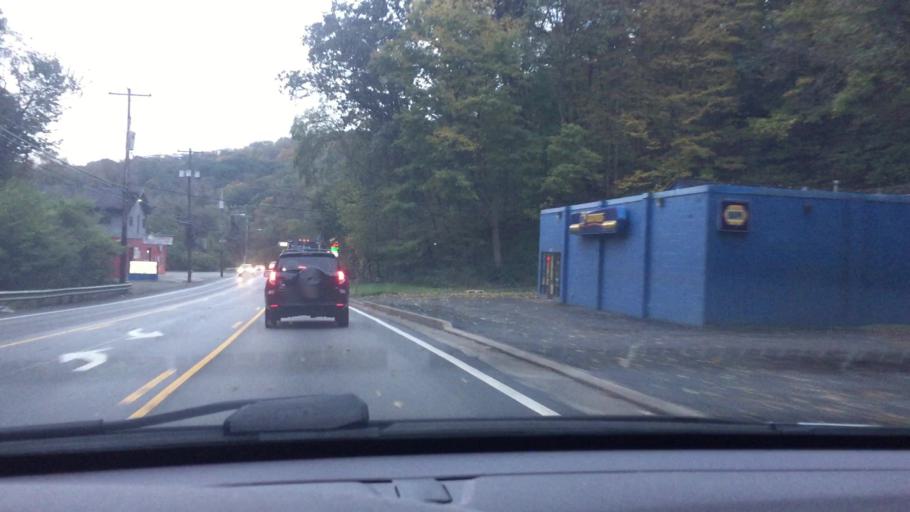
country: US
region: Pennsylvania
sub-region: Allegheny County
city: Ingram
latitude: 40.4413
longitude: -80.0942
